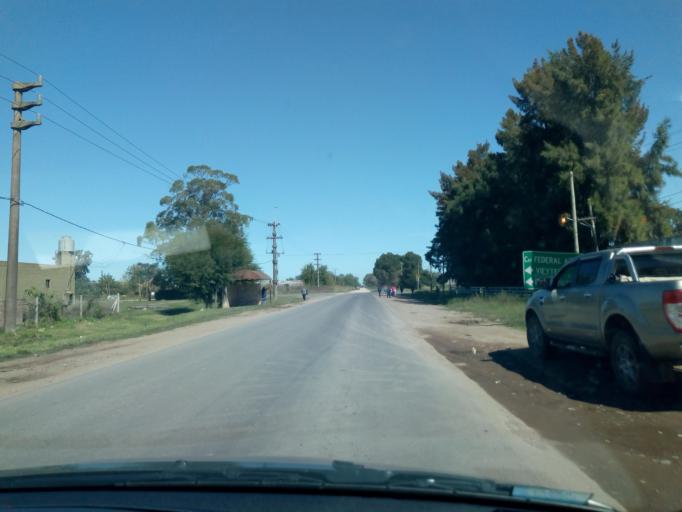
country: AR
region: Buenos Aires
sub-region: Partido de La Plata
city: La Plata
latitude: -35.0098
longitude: -58.0269
